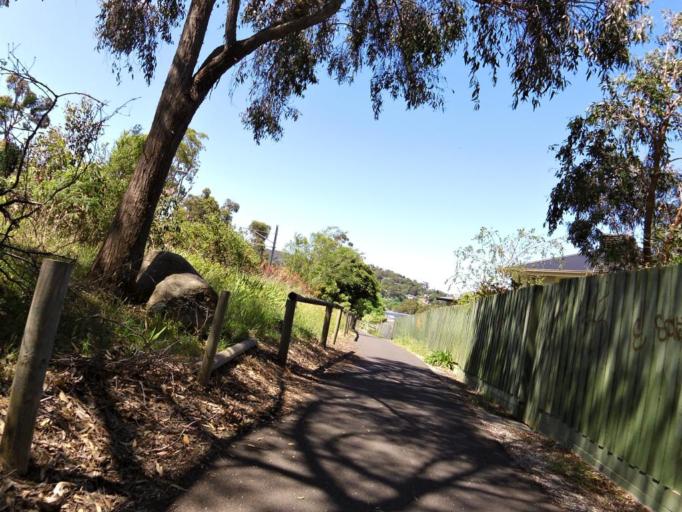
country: AU
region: Victoria
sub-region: Knox
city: Ferntree Gully
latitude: -37.8882
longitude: 145.2984
